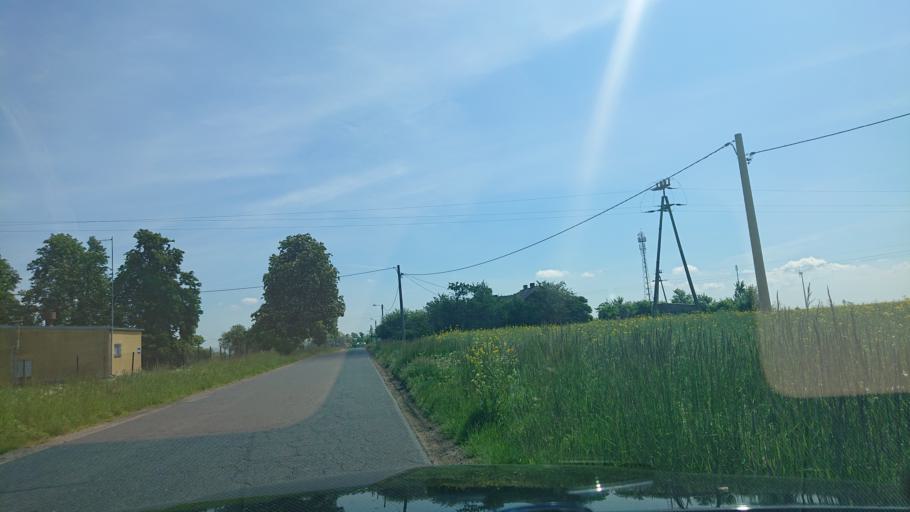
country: PL
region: Greater Poland Voivodeship
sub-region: Powiat gnieznienski
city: Niechanowo
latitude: 52.4549
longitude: 17.6055
